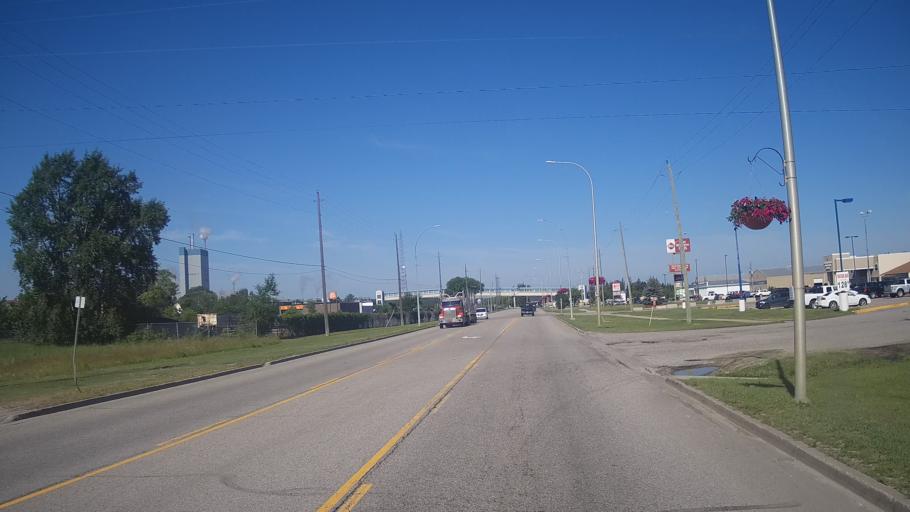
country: CA
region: Ontario
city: Dryden
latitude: 49.7865
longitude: -92.8314
